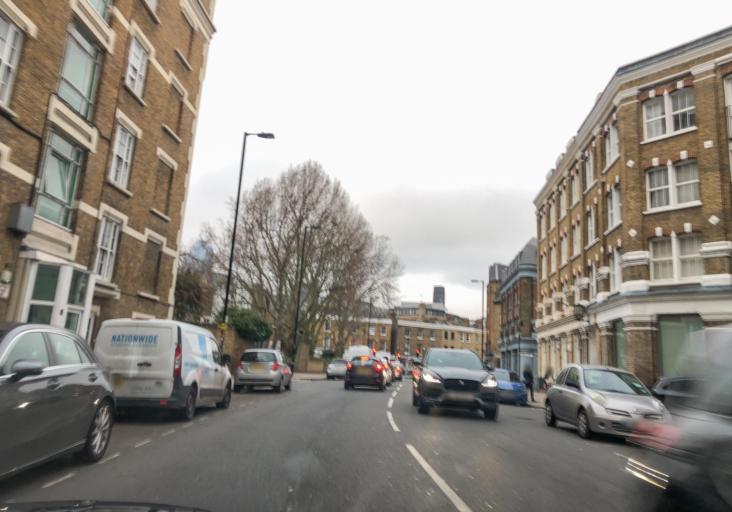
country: GB
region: England
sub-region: Greater London
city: City of London
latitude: 51.5021
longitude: -0.0955
